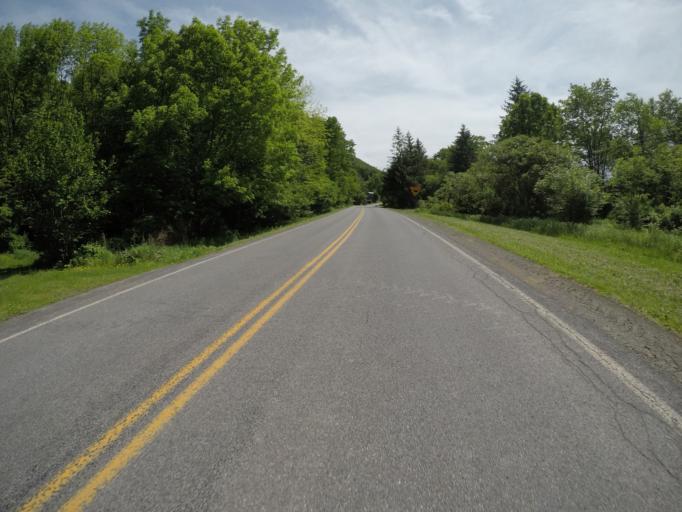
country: US
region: New York
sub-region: Delaware County
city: Delhi
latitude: 42.1362
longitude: -74.8011
